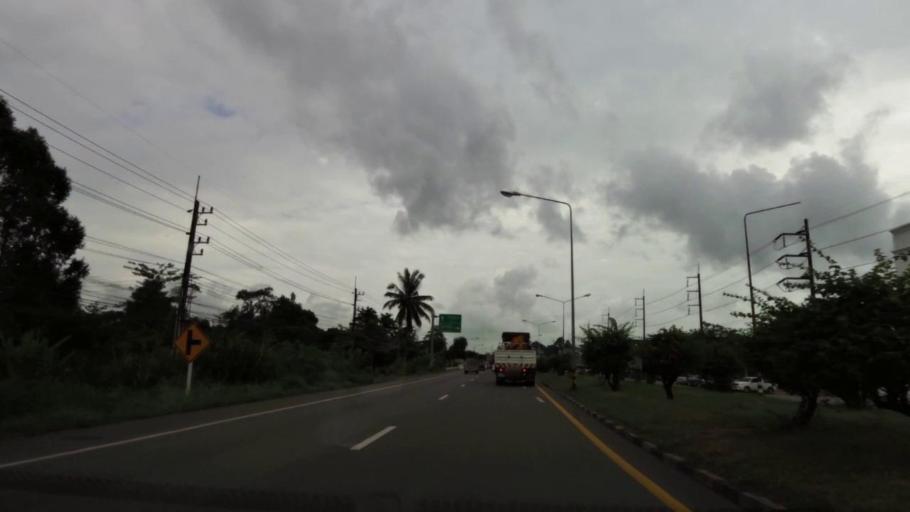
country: TH
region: Chanthaburi
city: Tha Mai
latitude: 12.7197
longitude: 101.9746
